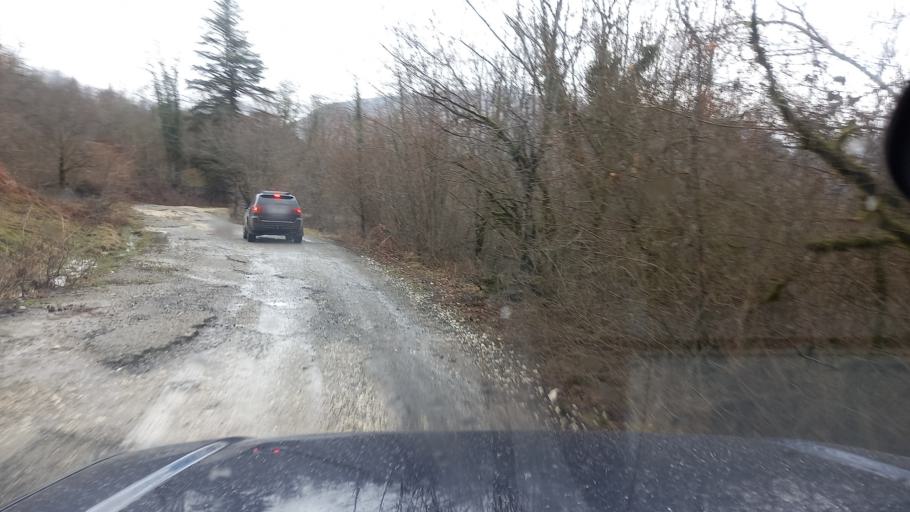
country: GE
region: Abkhazia
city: Dranda
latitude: 43.0313
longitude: 41.3230
